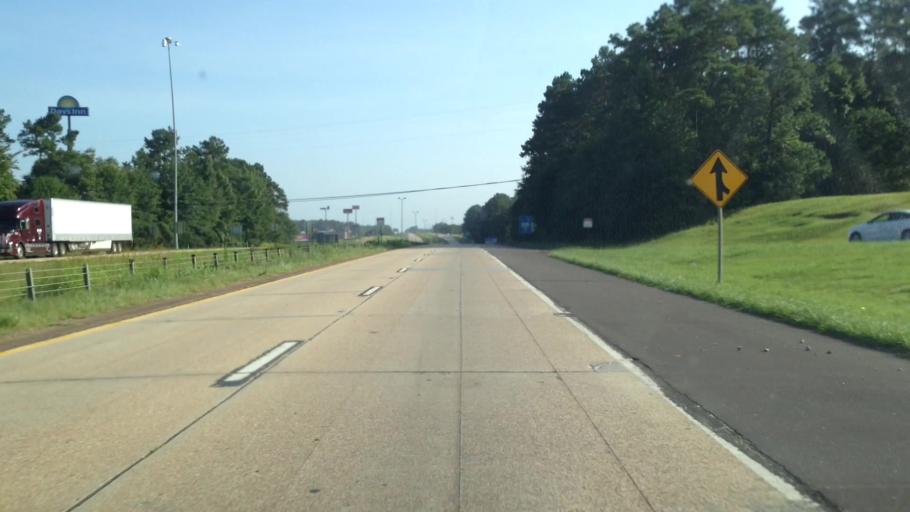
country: US
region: Mississippi
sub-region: Pike County
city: McComb
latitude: 31.2487
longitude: -90.4798
